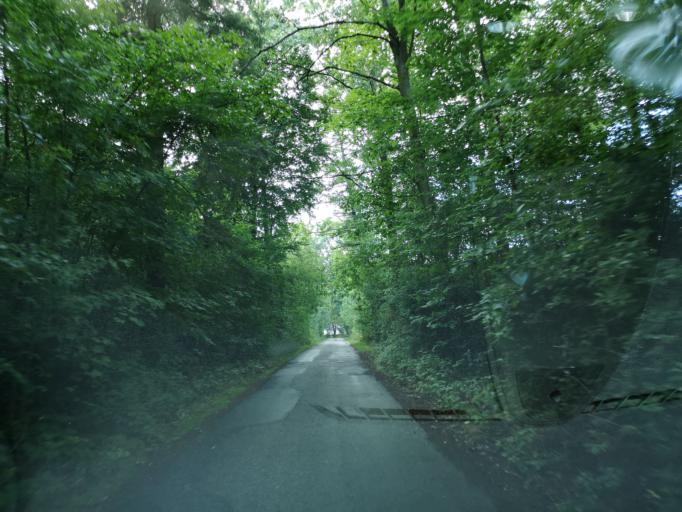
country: DK
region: Central Jutland
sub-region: Holstebro Kommune
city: Holstebro
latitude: 56.3357
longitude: 8.6382
